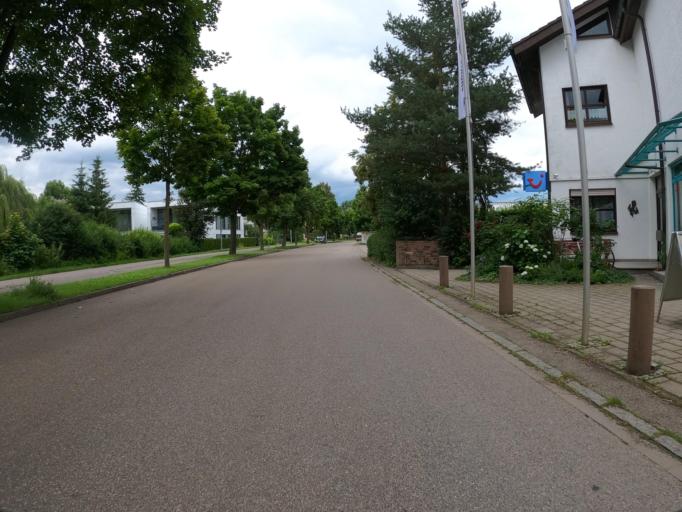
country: DE
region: Baden-Wuerttemberg
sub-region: Tuebingen Region
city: Langenau
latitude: 48.5001
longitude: 10.1296
